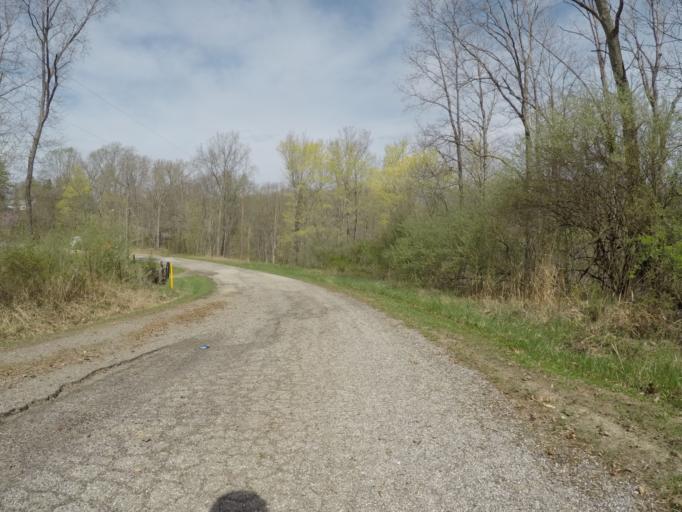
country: US
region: West Virginia
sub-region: Wayne County
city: Lavalette
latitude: 38.3310
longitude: -82.3604
